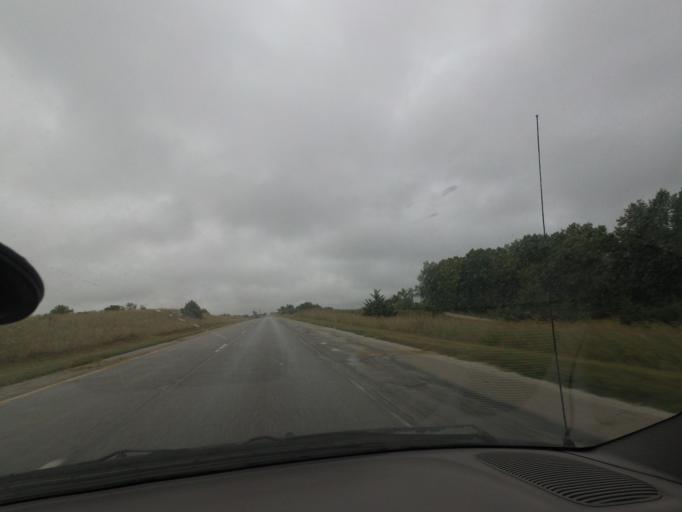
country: US
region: Illinois
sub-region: Pike County
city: Barry
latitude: 39.7333
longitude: -91.1245
